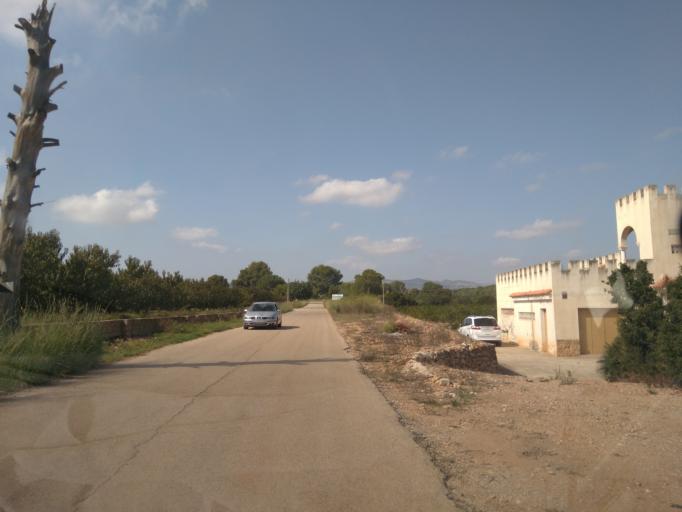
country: ES
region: Valencia
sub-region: Provincia de Valencia
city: Masalaves
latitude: 39.1715
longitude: -0.5548
